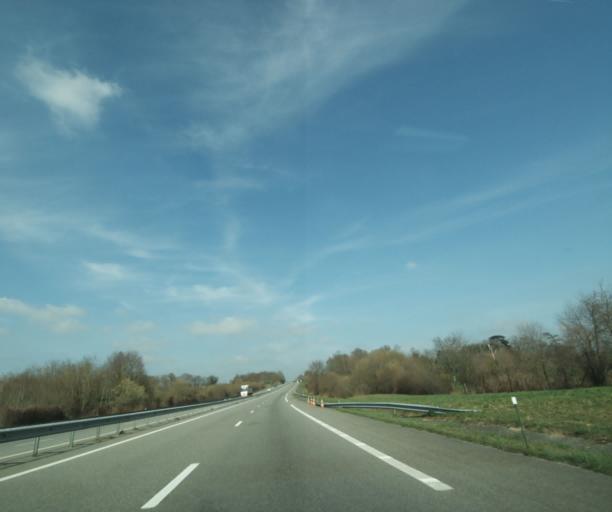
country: FR
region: Limousin
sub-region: Departement de la Haute-Vienne
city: Arnac-la-Poste
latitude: 46.2511
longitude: 1.3915
